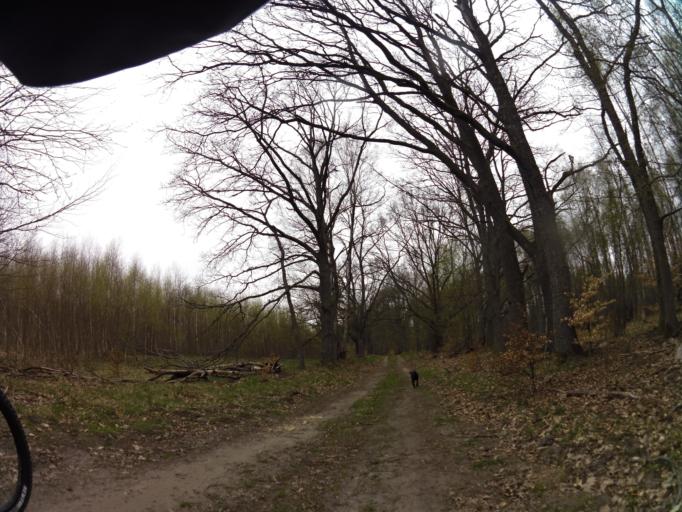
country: PL
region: West Pomeranian Voivodeship
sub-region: Powiat koszalinski
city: Bobolice
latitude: 53.9372
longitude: 16.7018
